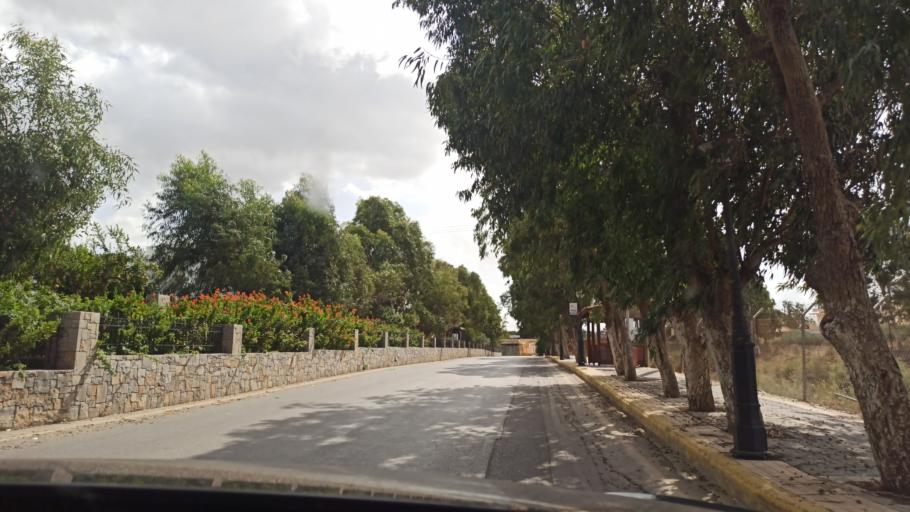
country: GR
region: Crete
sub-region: Nomos Irakleiou
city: Gazi
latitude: 35.3385
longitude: 25.0562
